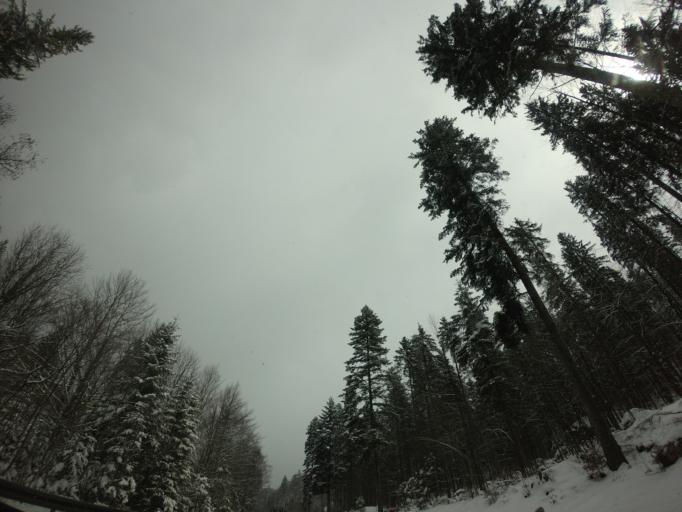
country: DE
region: Bavaria
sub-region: Upper Bavaria
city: Grainau
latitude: 47.4815
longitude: 11.0126
